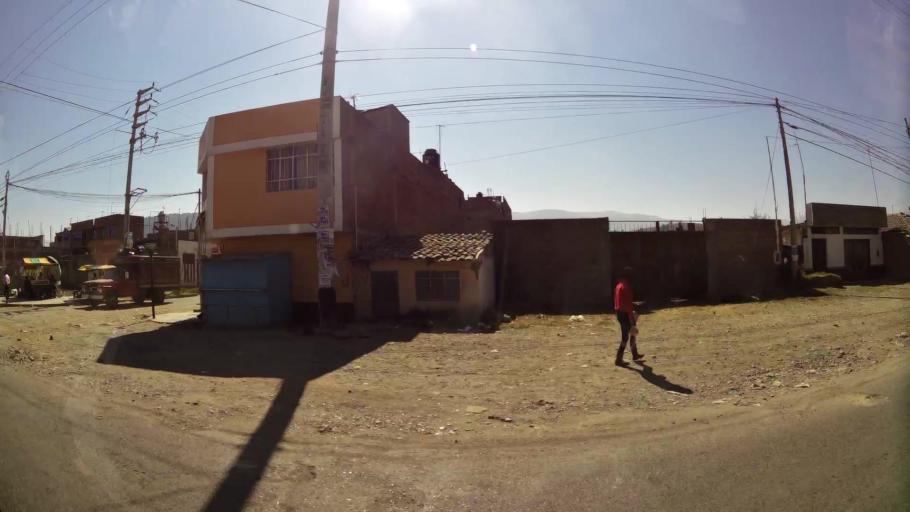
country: PE
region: Junin
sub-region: Provincia de Huancayo
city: San Agustin
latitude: -12.0013
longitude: -75.2518
